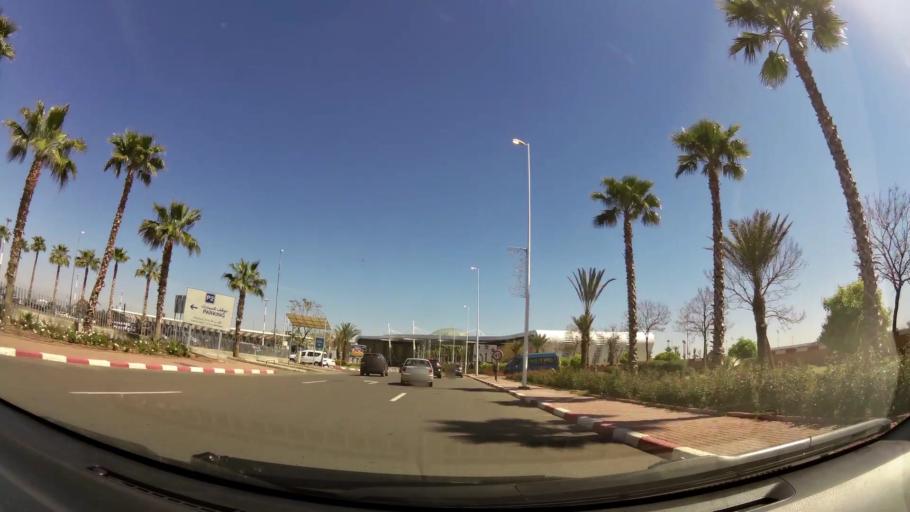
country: MA
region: Marrakech-Tensift-Al Haouz
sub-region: Marrakech
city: Marrakesh
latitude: 31.5983
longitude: -8.0258
